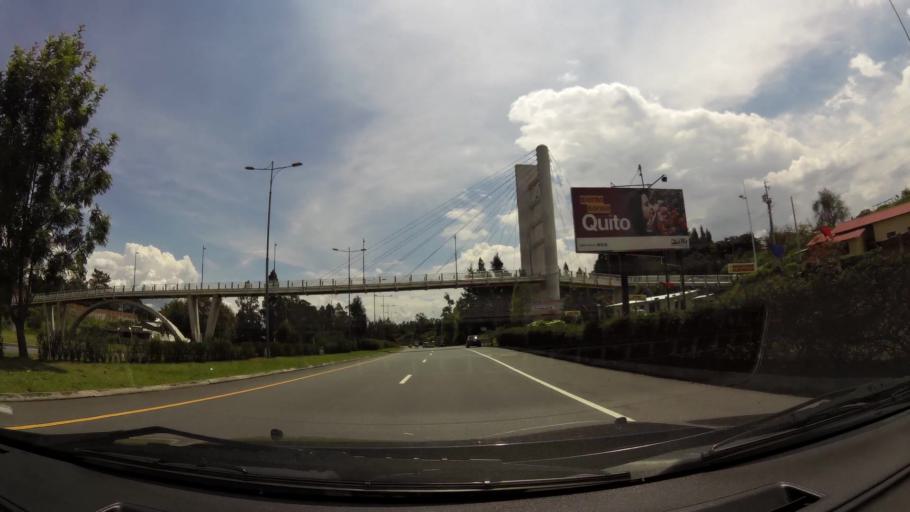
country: EC
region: Pichincha
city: Sangolqui
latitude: -0.1858
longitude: -78.3393
